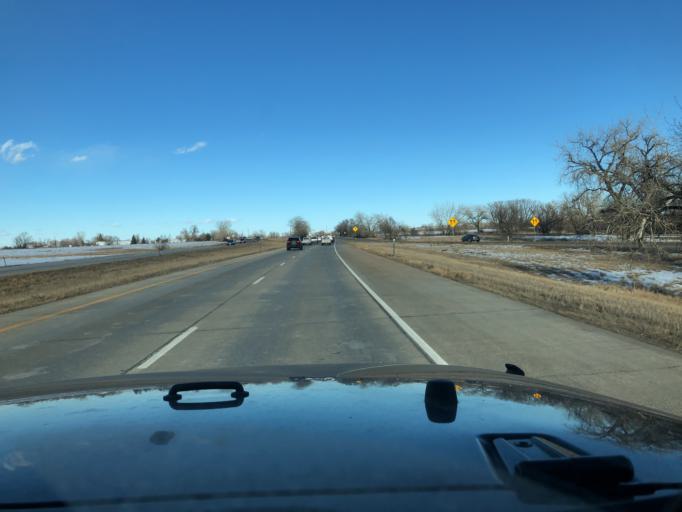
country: US
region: Colorado
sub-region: Boulder County
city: Boulder
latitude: 40.0458
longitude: -105.2398
